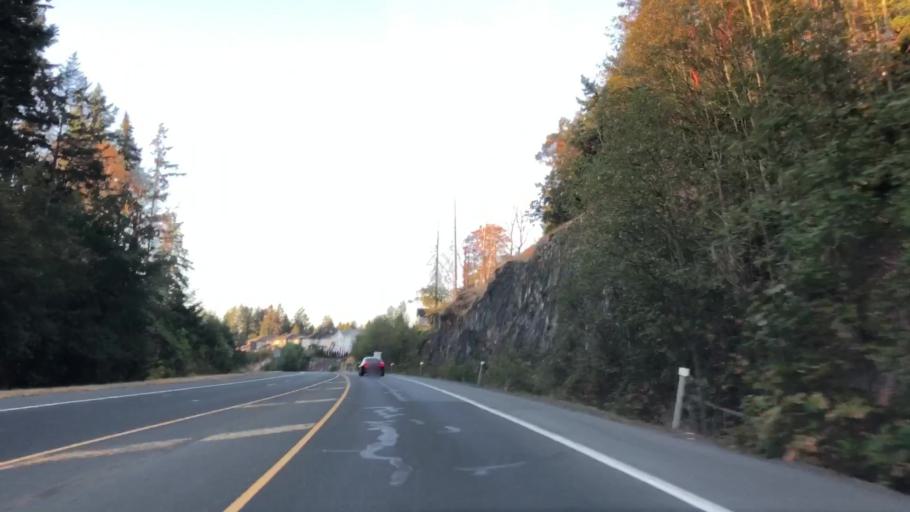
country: CA
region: British Columbia
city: Colwood
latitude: 48.4202
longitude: -123.5051
